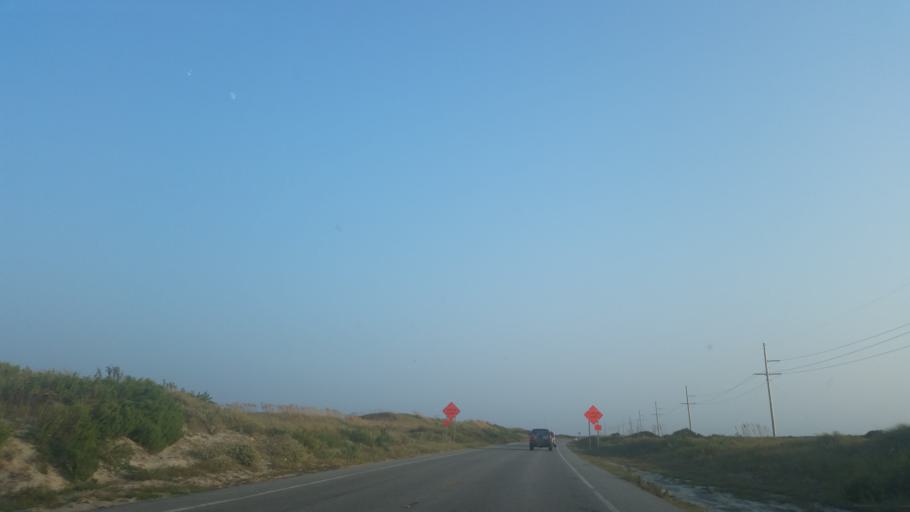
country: US
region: North Carolina
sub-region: Dare County
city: Wanchese
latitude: 35.6976
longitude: -75.4867
